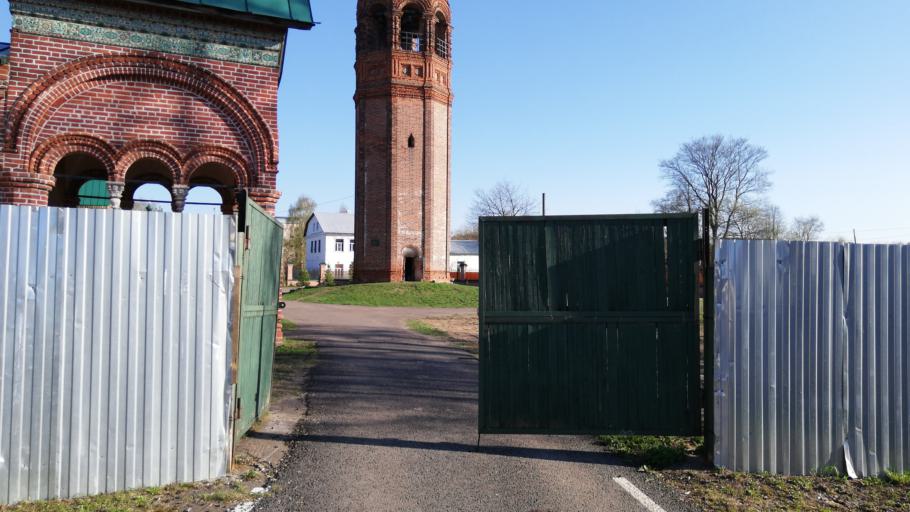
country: RU
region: Jaroslavl
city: Yaroslavl
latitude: 57.6116
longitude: 39.9055
